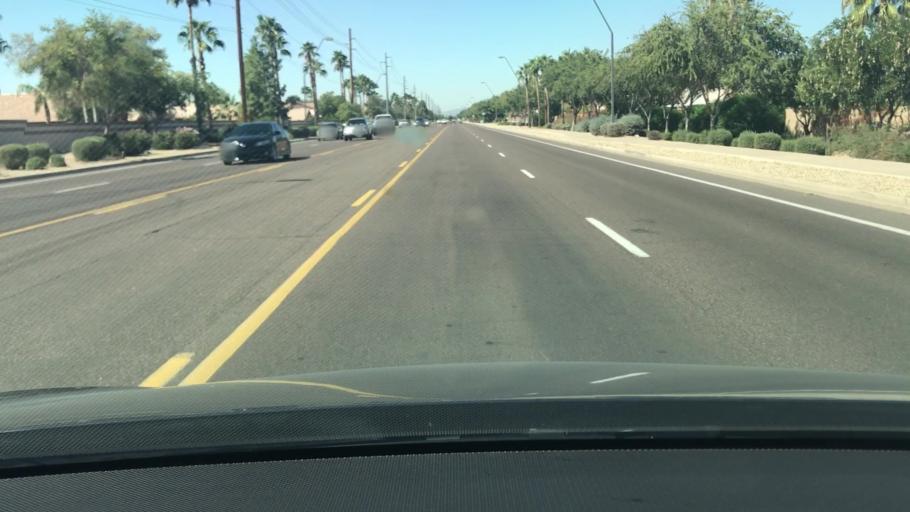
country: US
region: Arizona
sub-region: Maricopa County
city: Gilbert
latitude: 33.3210
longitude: -111.7919
